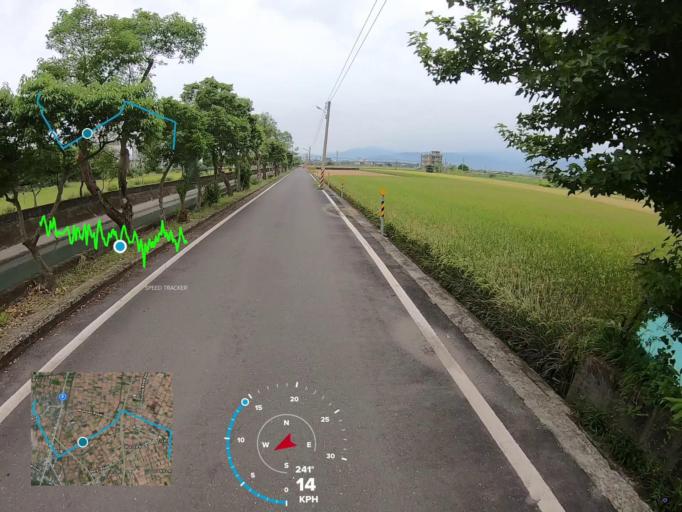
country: TW
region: Taiwan
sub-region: Yilan
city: Yilan
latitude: 24.7782
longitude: 121.7697
